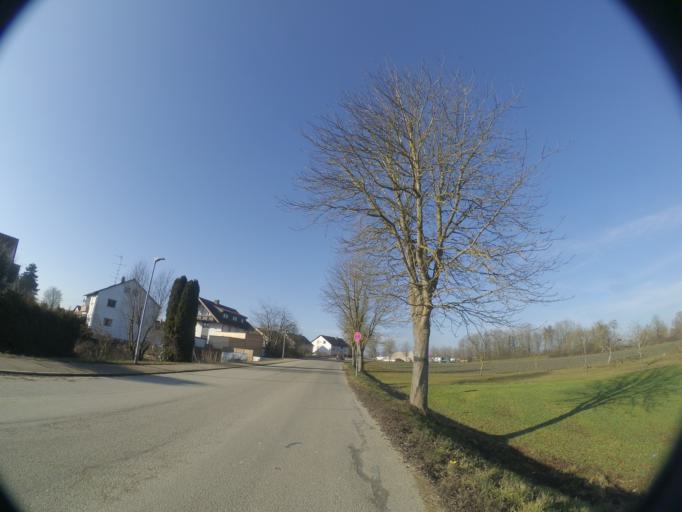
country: DE
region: Baden-Wuerttemberg
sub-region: Tuebingen Region
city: Dornstadt
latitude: 48.4722
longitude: 9.9424
